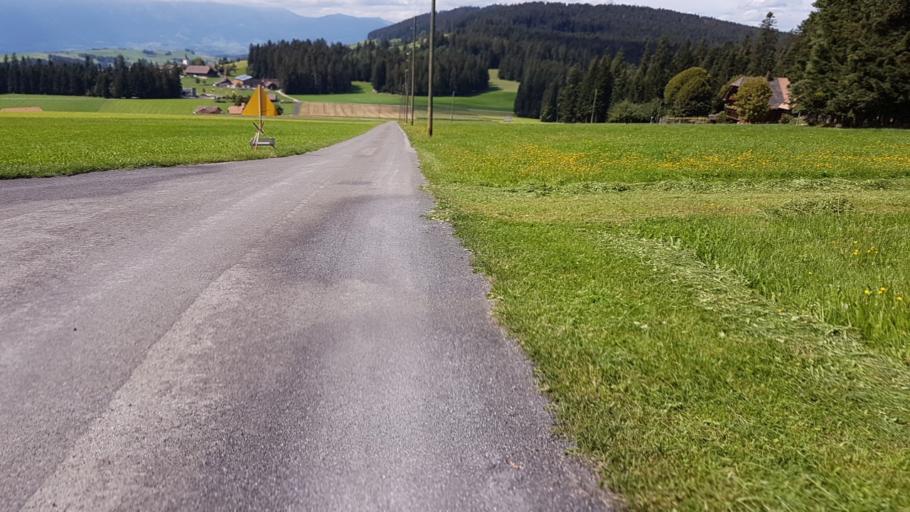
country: CH
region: Bern
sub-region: Bern-Mittelland District
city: Linden
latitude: 46.8366
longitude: 7.7103
